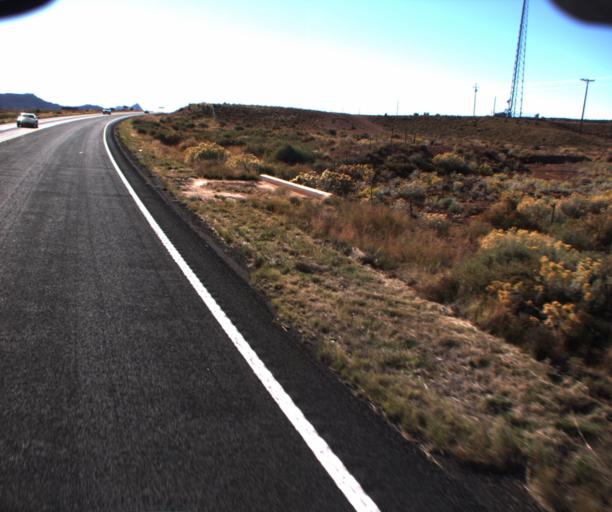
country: US
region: Arizona
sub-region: Coconino County
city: Tuba City
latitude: 36.3960
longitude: -111.5272
